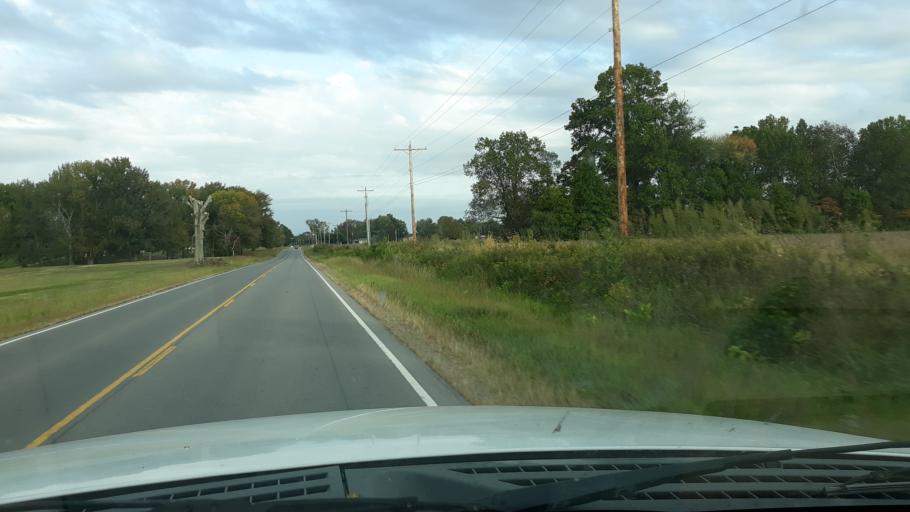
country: US
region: Illinois
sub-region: Saline County
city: Eldorado
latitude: 37.8217
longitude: -88.4916
